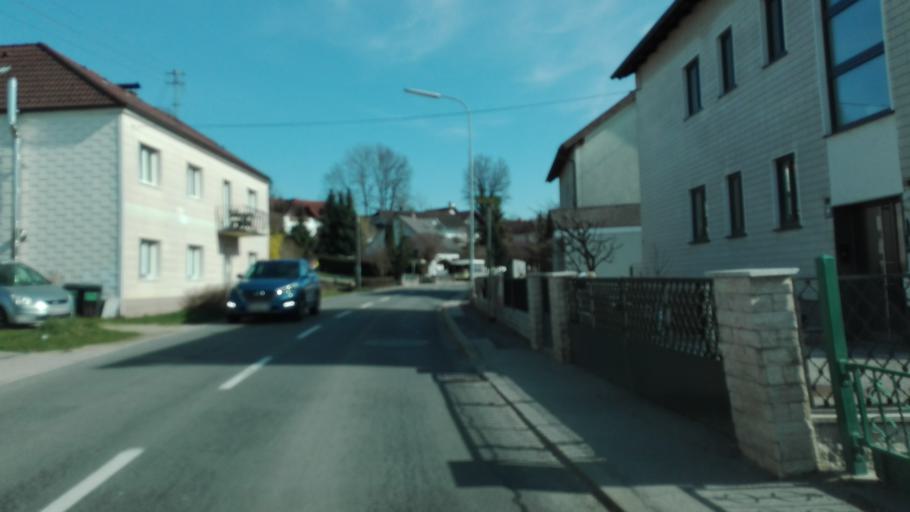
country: AT
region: Upper Austria
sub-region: Politischer Bezirk Perg
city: Perg
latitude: 48.2667
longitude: 14.5848
